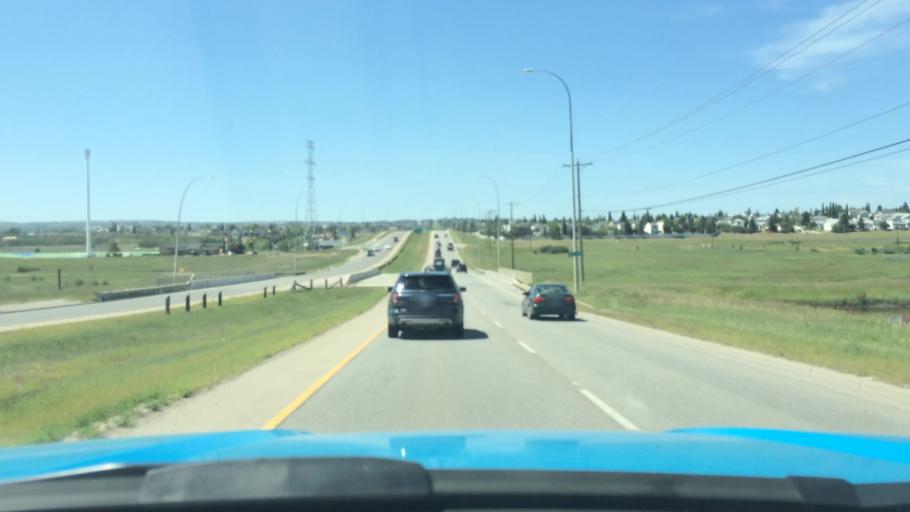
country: CA
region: Alberta
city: Calgary
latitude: 51.1540
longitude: -114.0323
